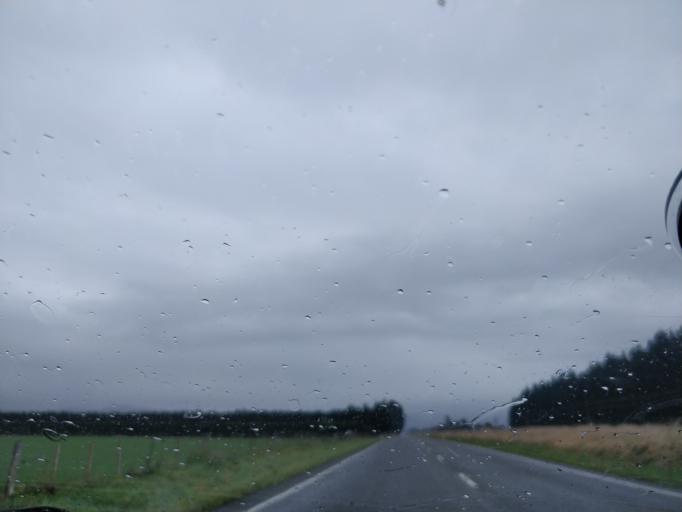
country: NZ
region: Canterbury
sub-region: Selwyn District
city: Darfield
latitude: -43.3803
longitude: 172.0045
